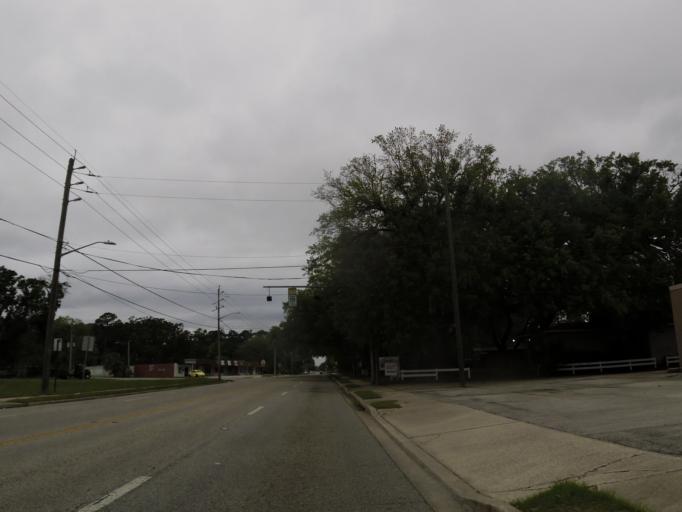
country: US
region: Florida
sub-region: Duval County
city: Jacksonville
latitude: 30.2632
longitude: -81.6292
